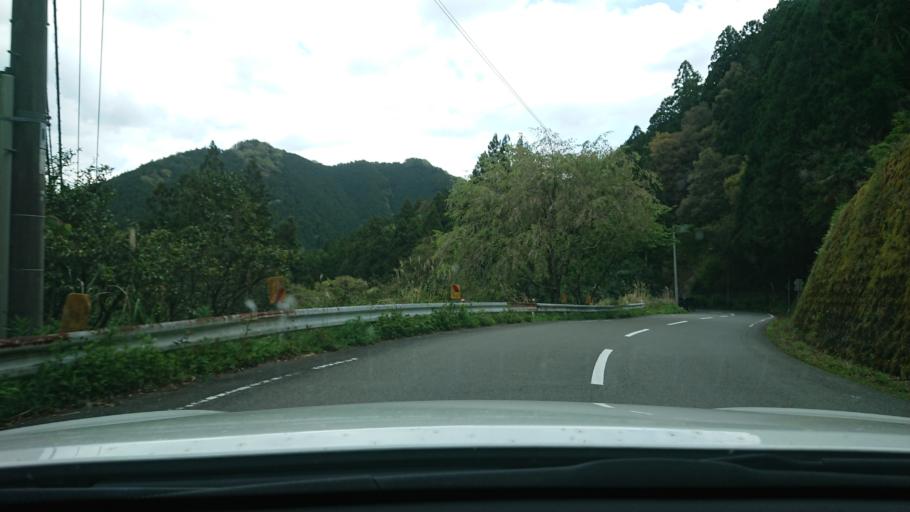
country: JP
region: Tokushima
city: Ishii
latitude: 33.9163
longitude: 134.4230
